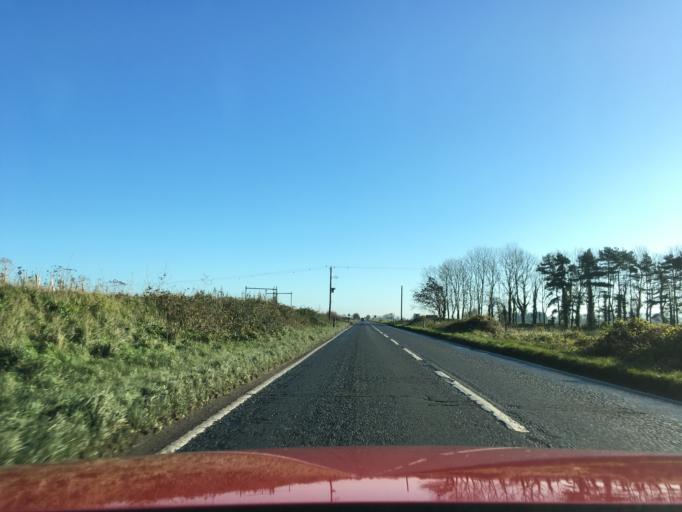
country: GB
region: England
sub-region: Somerset
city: Westonzoyland
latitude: 51.1053
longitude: -2.9090
